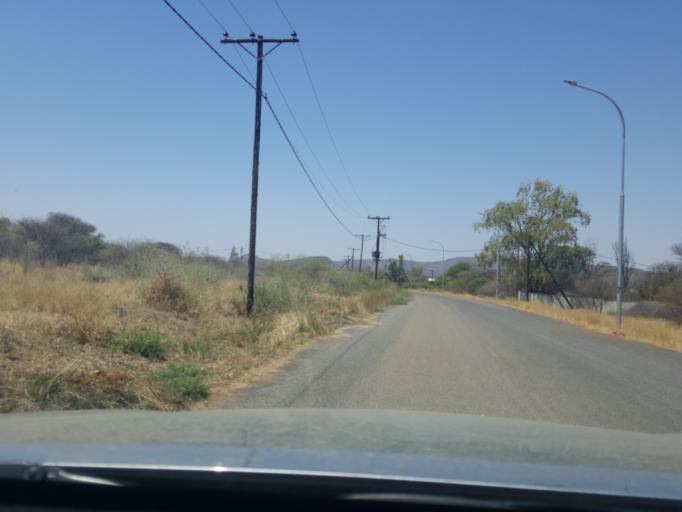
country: BW
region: South East
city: Lobatse
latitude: -25.1907
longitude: 25.6736
